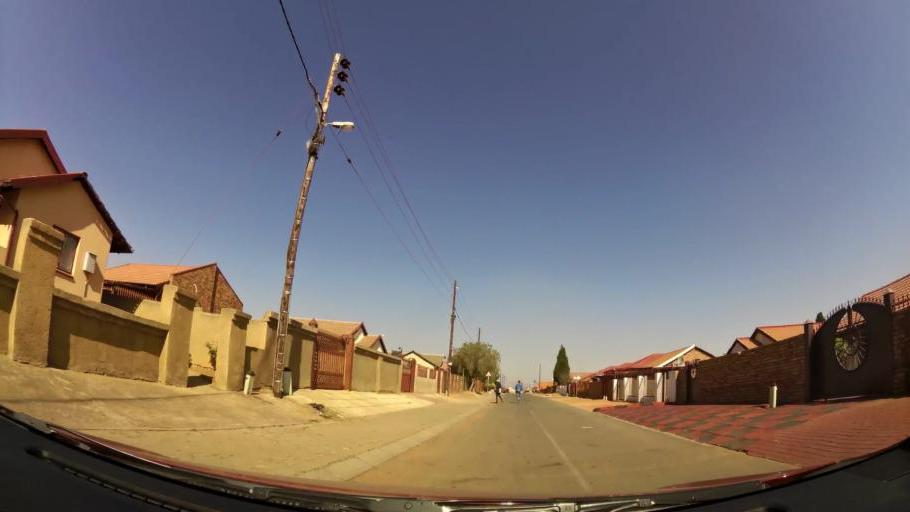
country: ZA
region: Gauteng
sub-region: City of Tshwane Metropolitan Municipality
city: Mabopane
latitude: -25.5521
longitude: 28.0812
